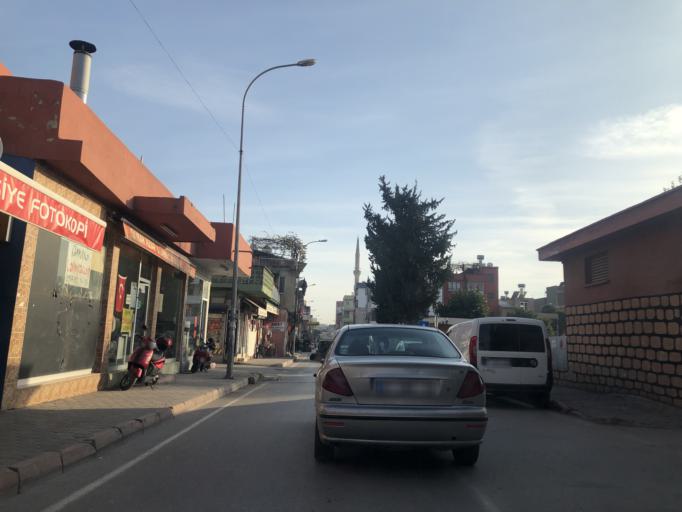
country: TR
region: Adana
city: Adana
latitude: 37.0167
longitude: 35.3144
